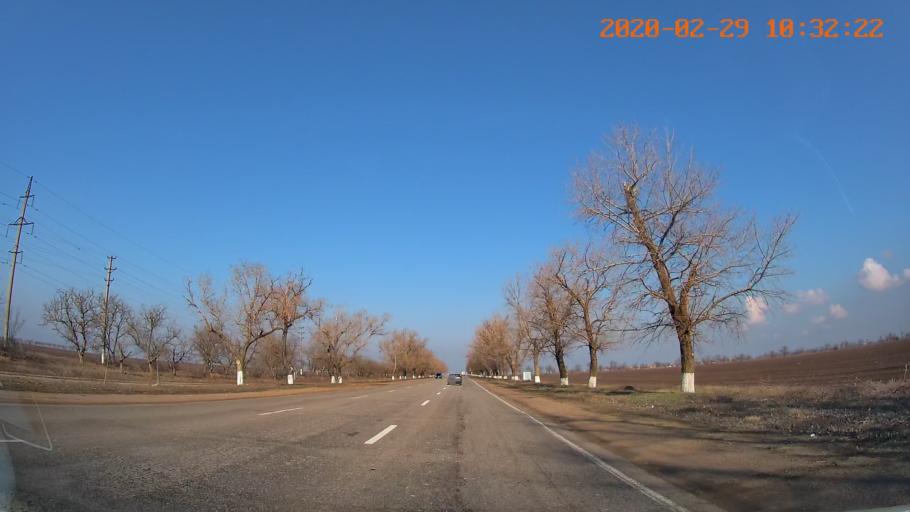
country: UA
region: Odessa
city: Velykoploske
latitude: 46.9602
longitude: 29.5544
